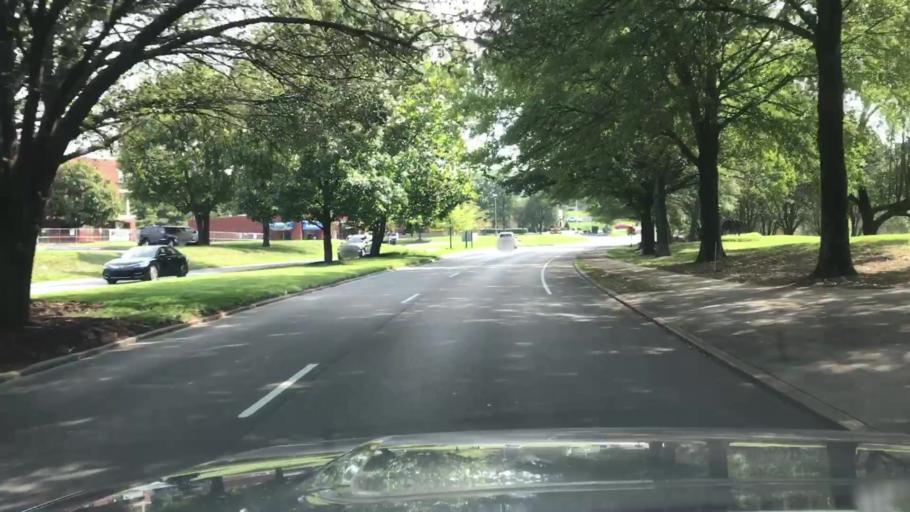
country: US
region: Tennessee
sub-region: Williamson County
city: Brentwood
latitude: 36.0341
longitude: -86.7944
